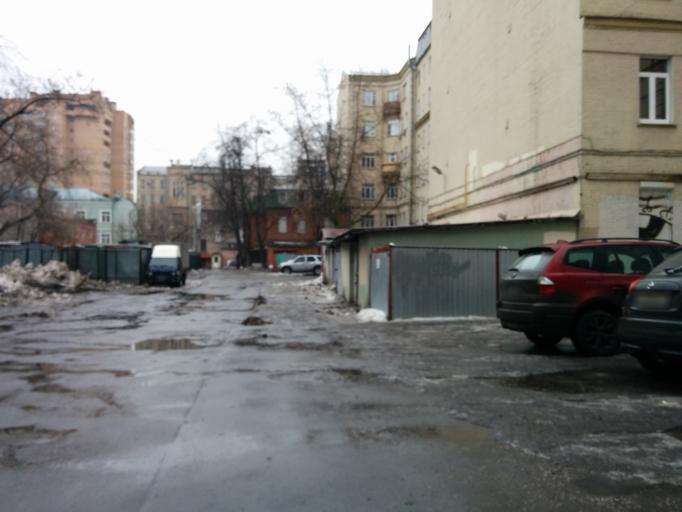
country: RU
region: Moscow
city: Mar'ina Roshcha
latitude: 55.7770
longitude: 37.6001
